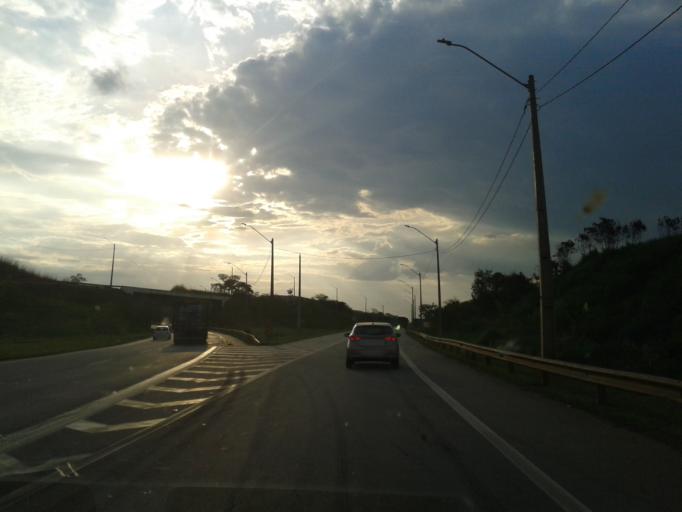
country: BR
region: Minas Gerais
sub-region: Betim
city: Betim
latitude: -19.9873
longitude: -44.1991
